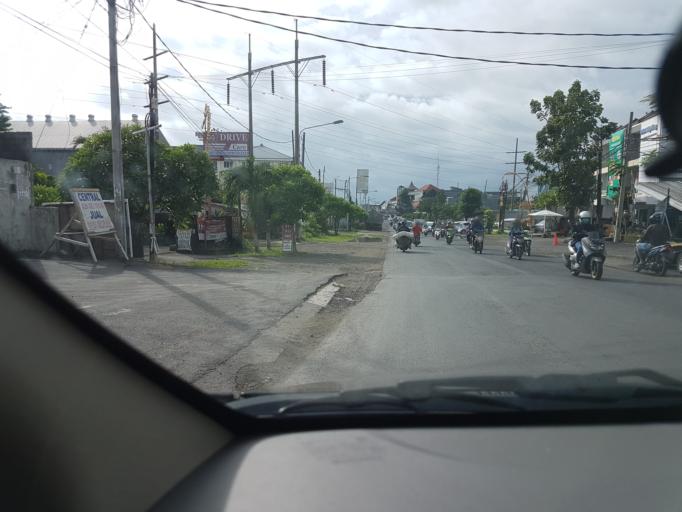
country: ID
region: Bali
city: Karyadharma
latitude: -8.6789
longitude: 115.1872
